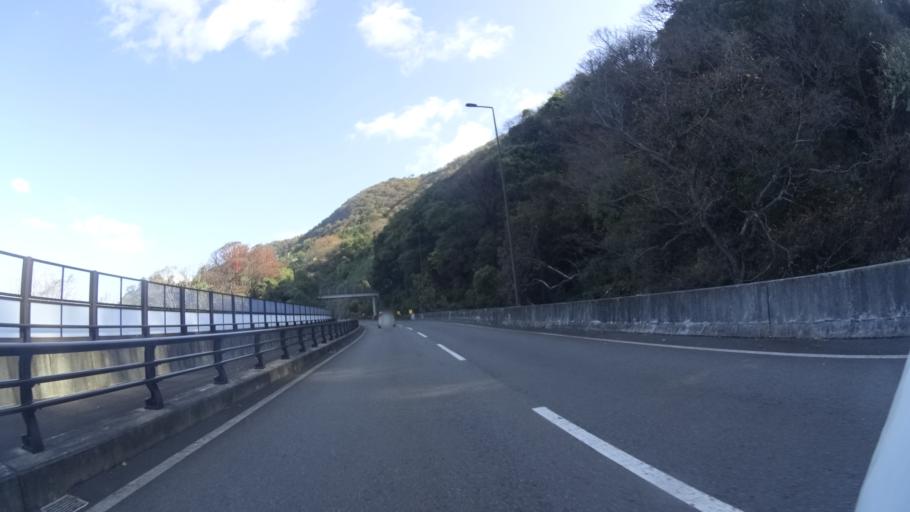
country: JP
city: Asahi
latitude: 35.9145
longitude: 135.9960
